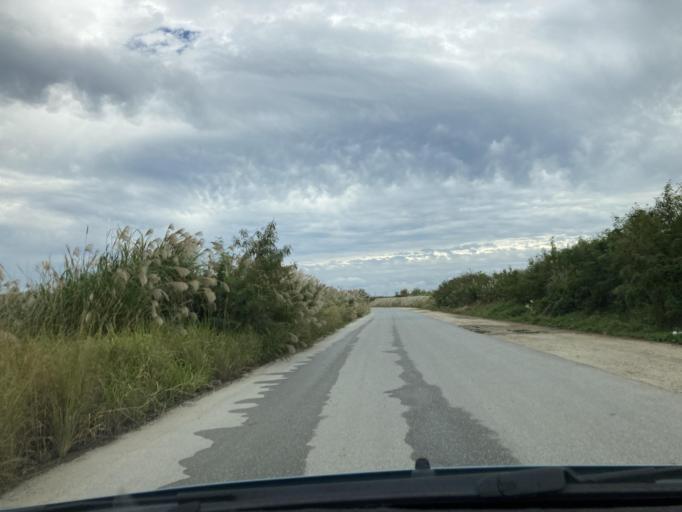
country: JP
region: Okinawa
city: Okinawa
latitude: 26.3867
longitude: 127.7436
